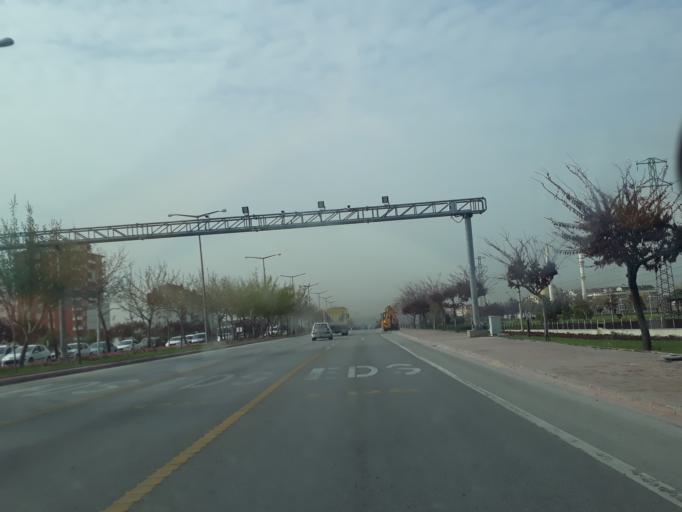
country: TR
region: Konya
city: Asagipinarbasi
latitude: 37.9928
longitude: 32.5185
